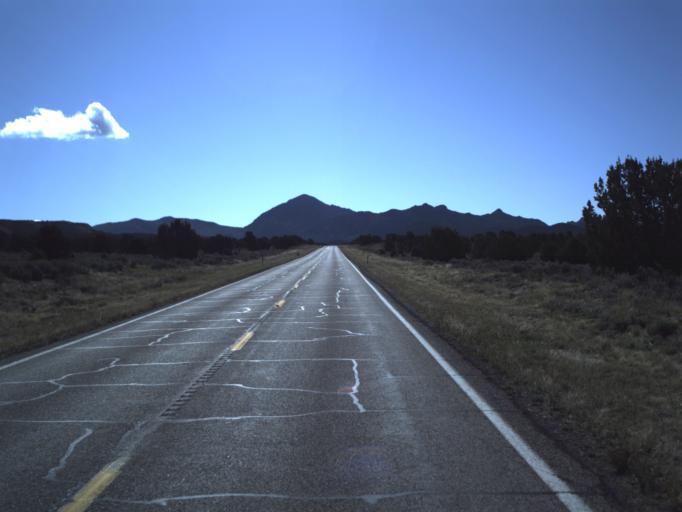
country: US
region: Utah
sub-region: Washington County
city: Enterprise
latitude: 37.6327
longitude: -113.4289
